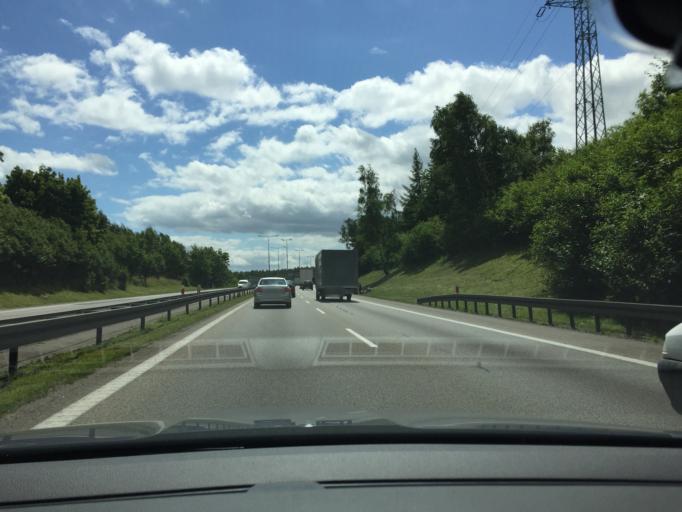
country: PL
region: Pomeranian Voivodeship
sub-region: Gdynia
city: Wielki Kack
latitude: 54.5041
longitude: 18.4607
